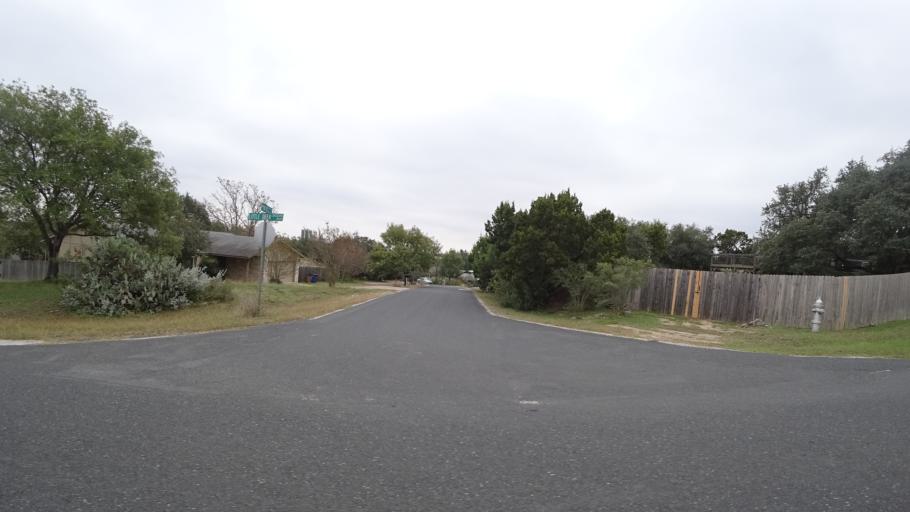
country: US
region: Texas
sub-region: Travis County
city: Barton Creek
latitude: 30.2415
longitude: -97.8903
